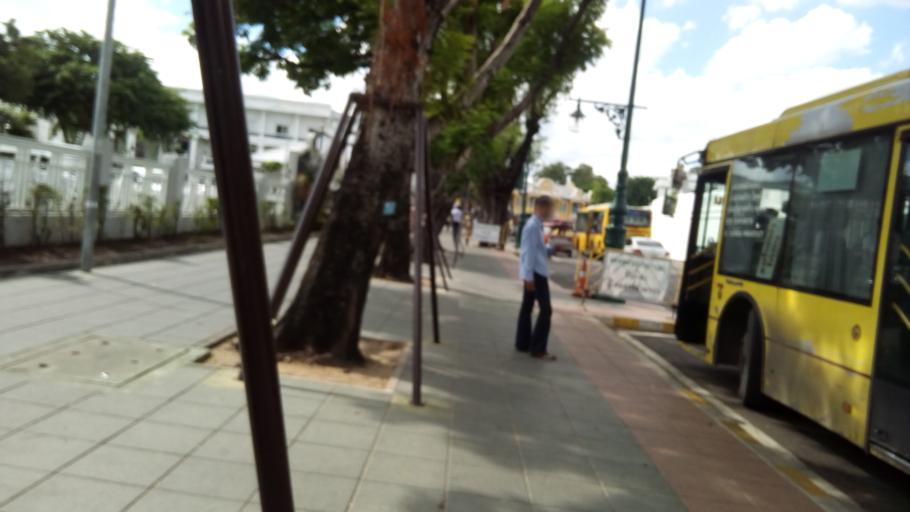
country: TH
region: Bangkok
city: Bangkok
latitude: 13.7511
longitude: 100.4894
